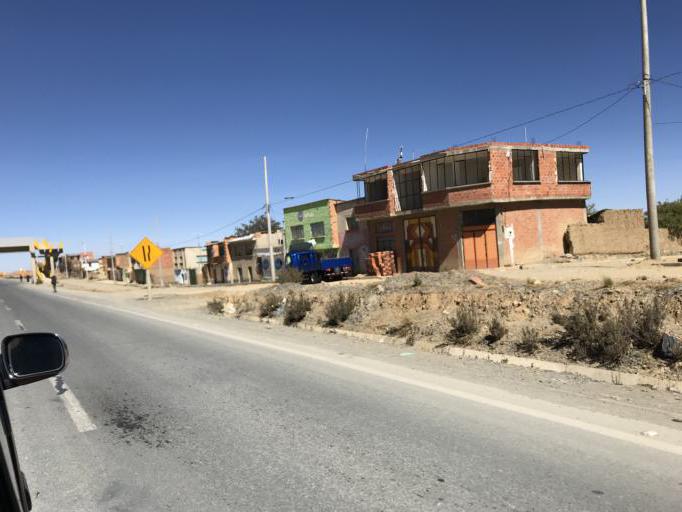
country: BO
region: La Paz
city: Batallas
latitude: -16.3354
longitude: -68.4163
